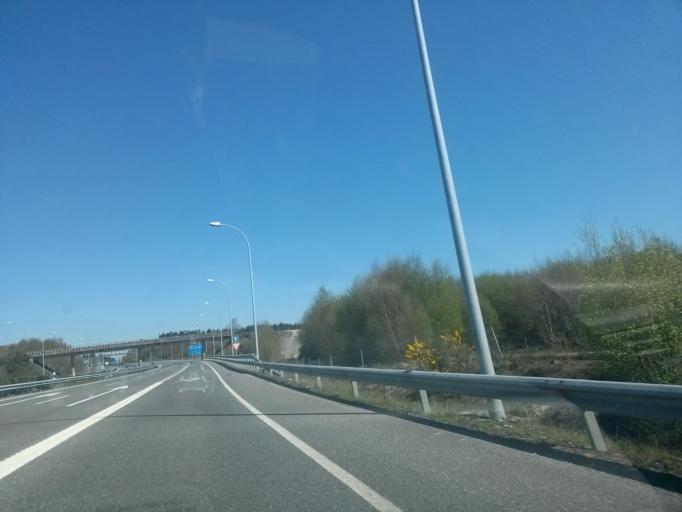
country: ES
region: Galicia
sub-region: Provincia de Lugo
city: Lugo
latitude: 43.0165
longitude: -7.5195
